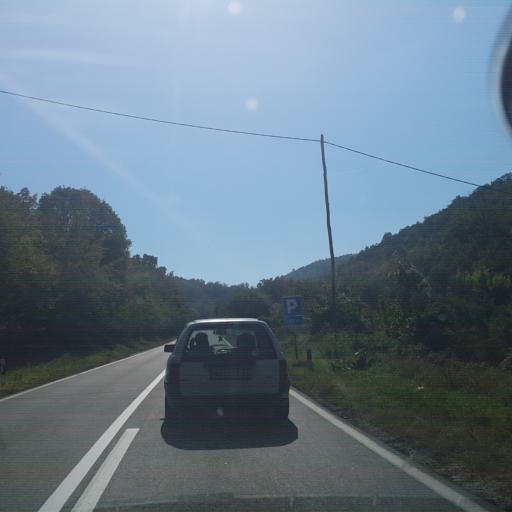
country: RS
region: Central Serbia
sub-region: Zajecarski Okrug
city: Knjazevac
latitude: 43.5437
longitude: 22.2328
